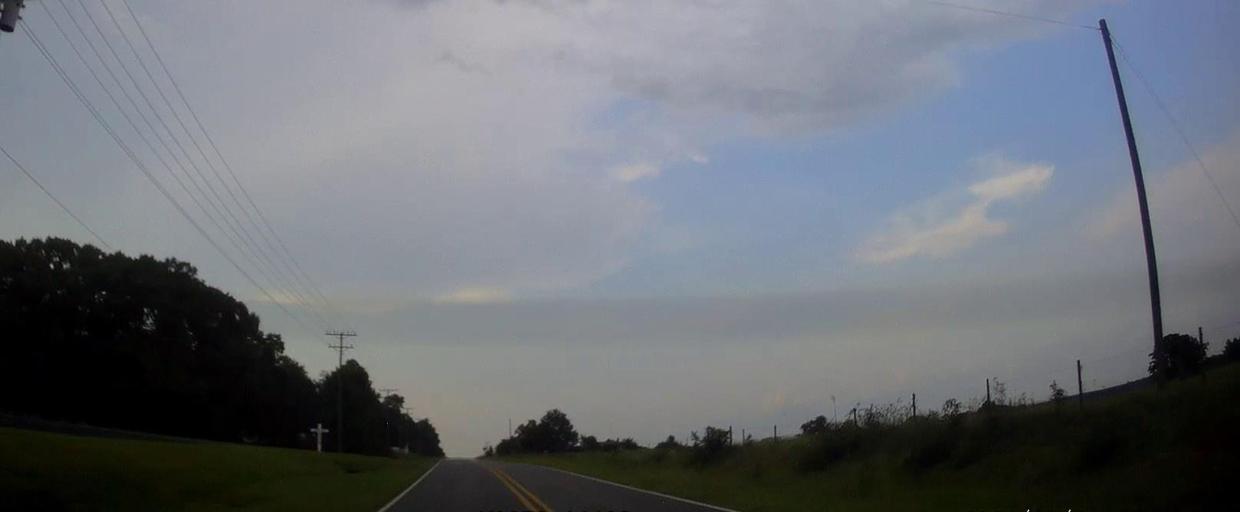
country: US
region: Georgia
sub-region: Laurens County
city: East Dublin
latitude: 32.5348
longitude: -82.8356
